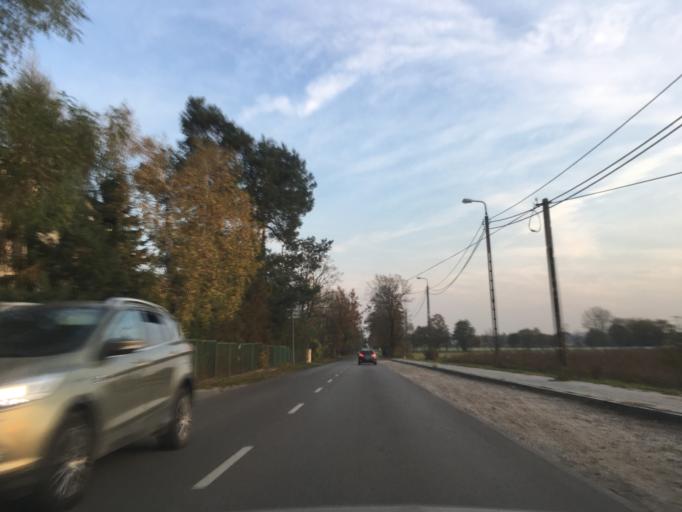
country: PL
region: Masovian Voivodeship
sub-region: Powiat piaseczynski
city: Lesznowola
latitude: 52.0579
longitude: 20.9211
